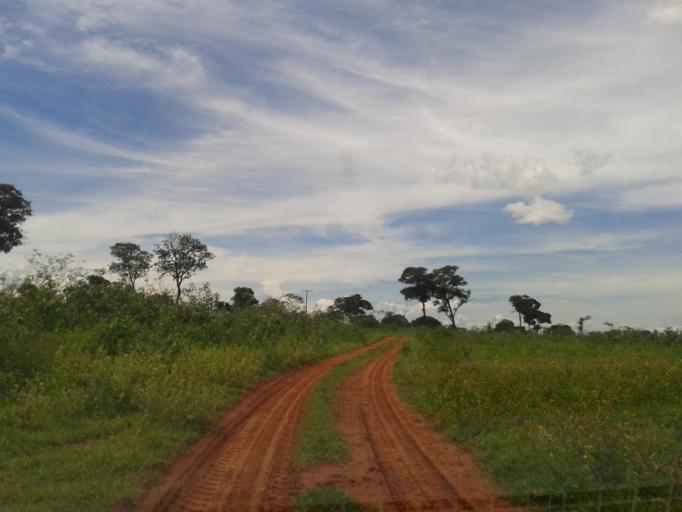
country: BR
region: Minas Gerais
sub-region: Santa Vitoria
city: Santa Vitoria
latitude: -19.1978
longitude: -50.5150
